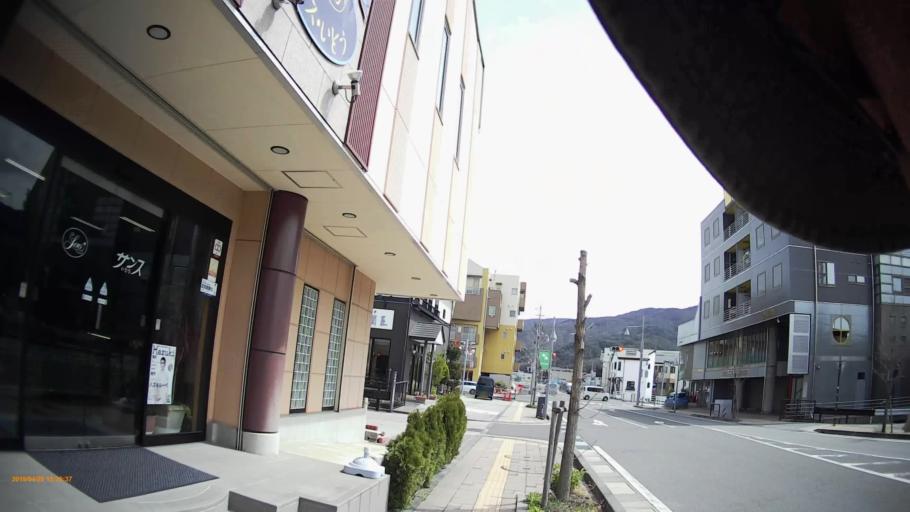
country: JP
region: Nagano
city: Chino
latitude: 35.9919
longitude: 138.1527
